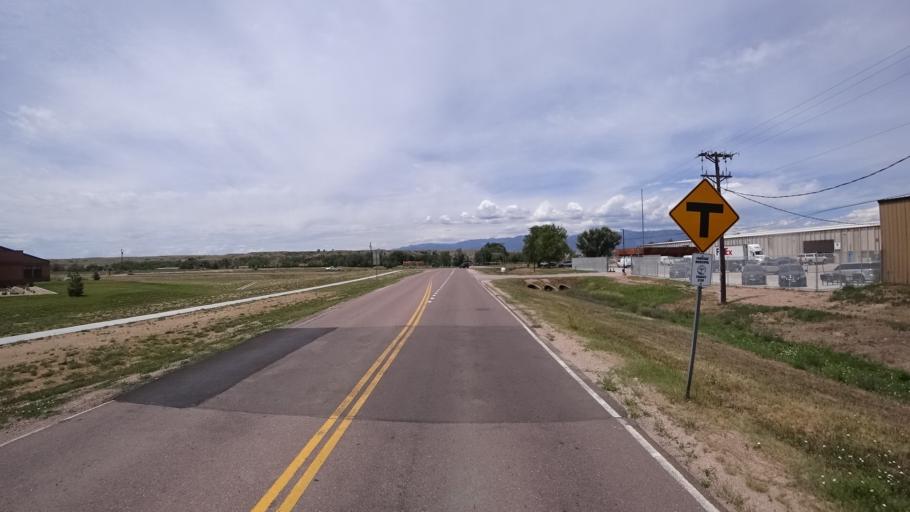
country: US
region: Colorado
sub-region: El Paso County
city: Fountain
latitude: 38.6644
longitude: -104.6910
